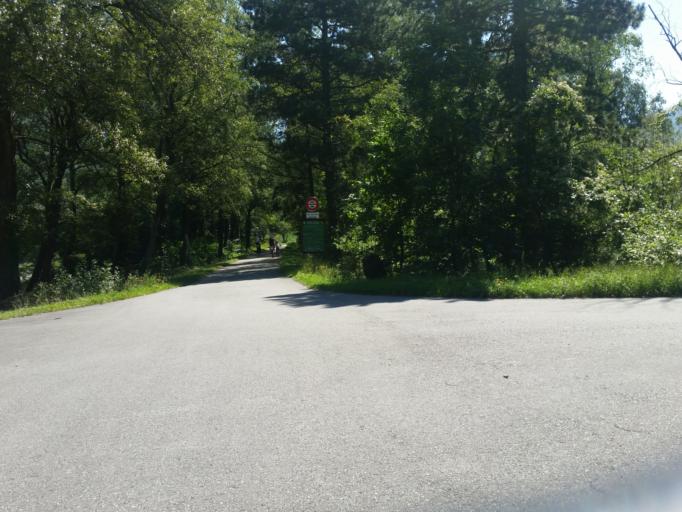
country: CH
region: Valais
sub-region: Saint-Maurice District
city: Vernayaz
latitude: 46.1411
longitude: 7.0470
